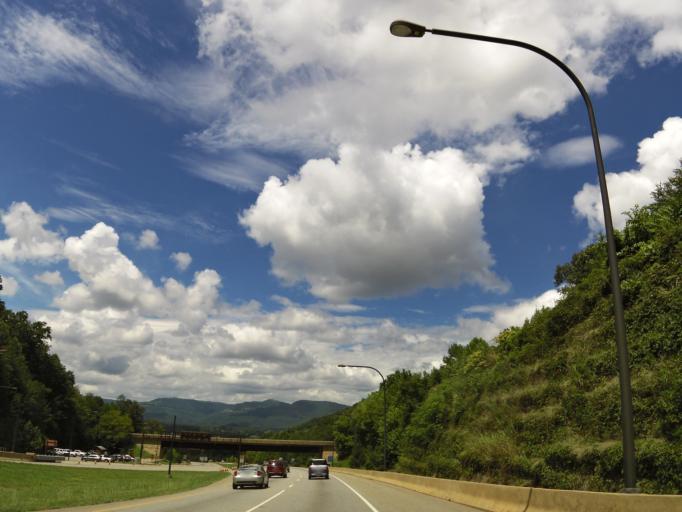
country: US
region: Kentucky
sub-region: Bell County
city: Middlesboro
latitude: 36.6037
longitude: -83.6848
